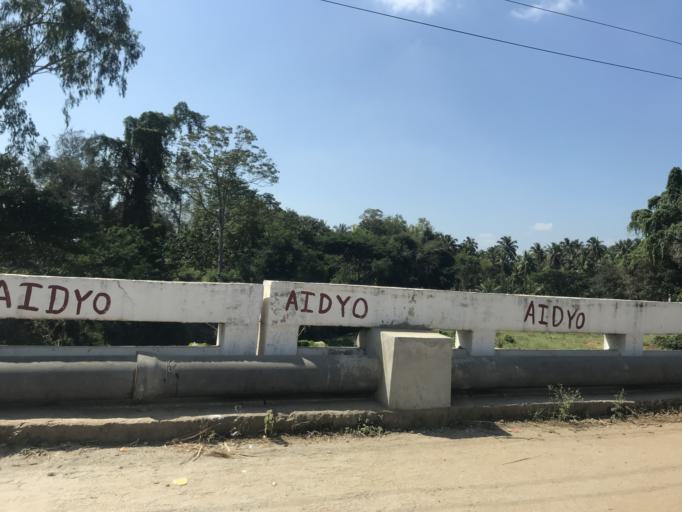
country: IN
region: Karnataka
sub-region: Mysore
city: Heggadadevankote
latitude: 12.0849
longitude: 76.3343
